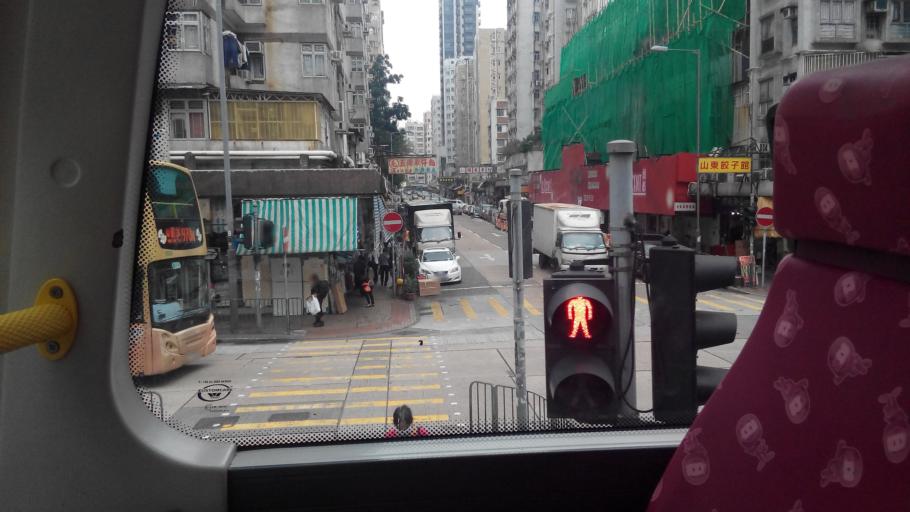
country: HK
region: Sham Shui Po
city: Sham Shui Po
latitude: 22.3369
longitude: 114.1594
